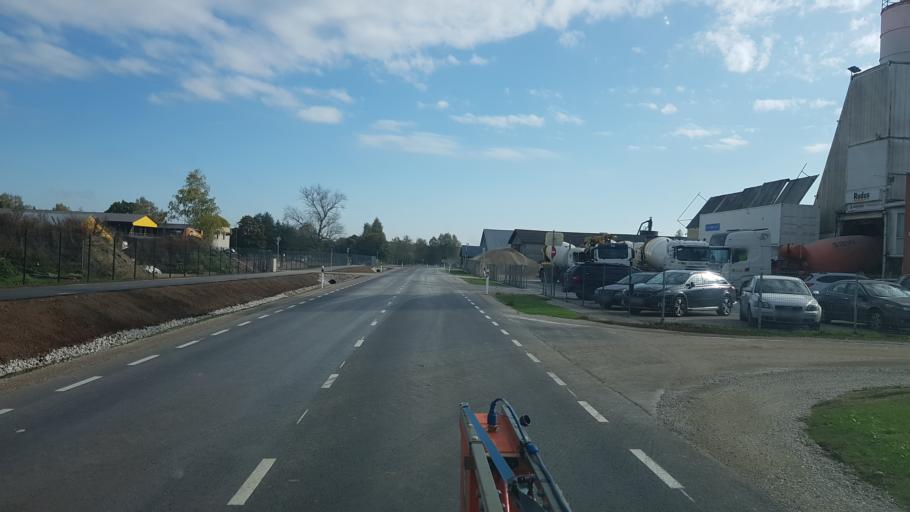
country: EE
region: Tartu
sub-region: UElenurme vald
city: Ulenurme
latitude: 58.2939
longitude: 26.7102
